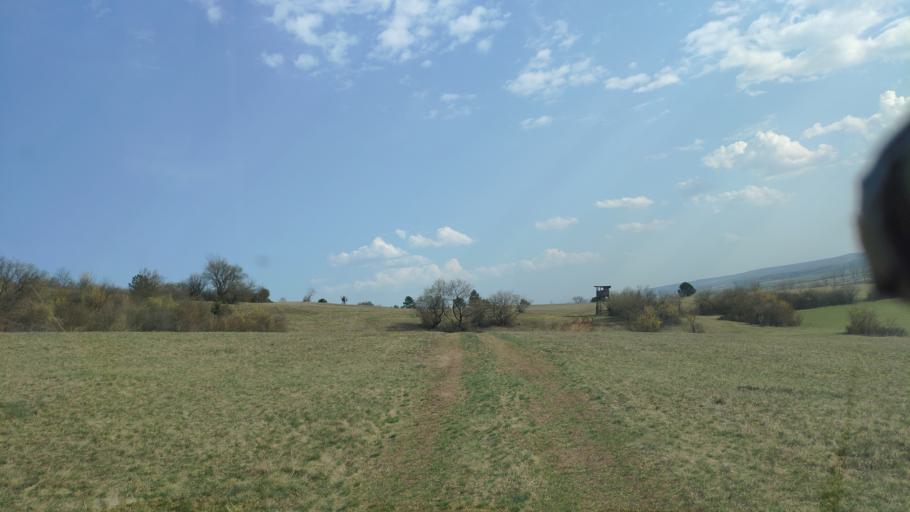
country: SK
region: Kosicky
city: Medzev
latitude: 48.6217
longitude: 20.9063
